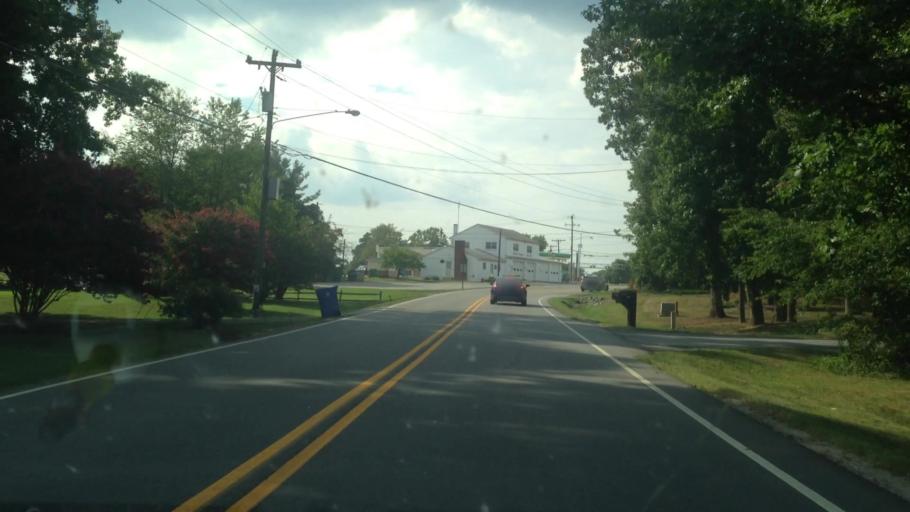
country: US
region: North Carolina
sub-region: Forsyth County
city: Kernersville
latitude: 36.1323
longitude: -80.1171
